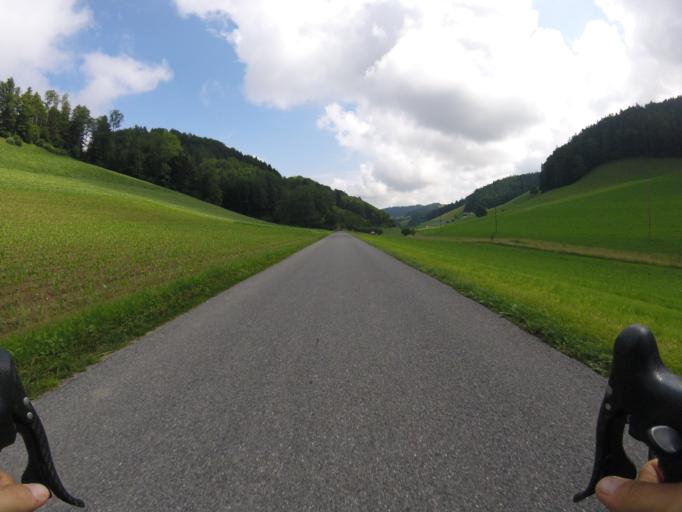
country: CH
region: Bern
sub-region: Emmental District
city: Krauchthal
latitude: 46.9917
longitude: 7.5818
